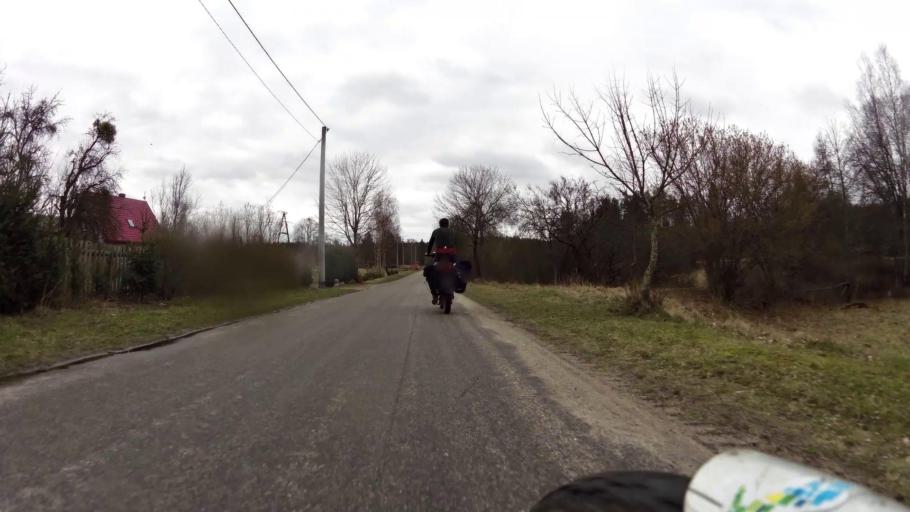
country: PL
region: Pomeranian Voivodeship
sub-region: Powiat bytowski
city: Trzebielino
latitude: 54.0803
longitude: 17.1179
